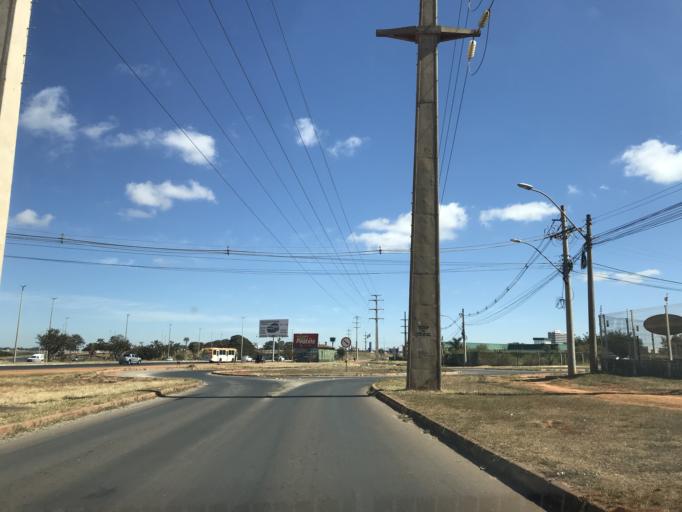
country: BR
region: Federal District
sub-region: Brasilia
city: Brasilia
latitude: -15.8762
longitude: -48.0235
